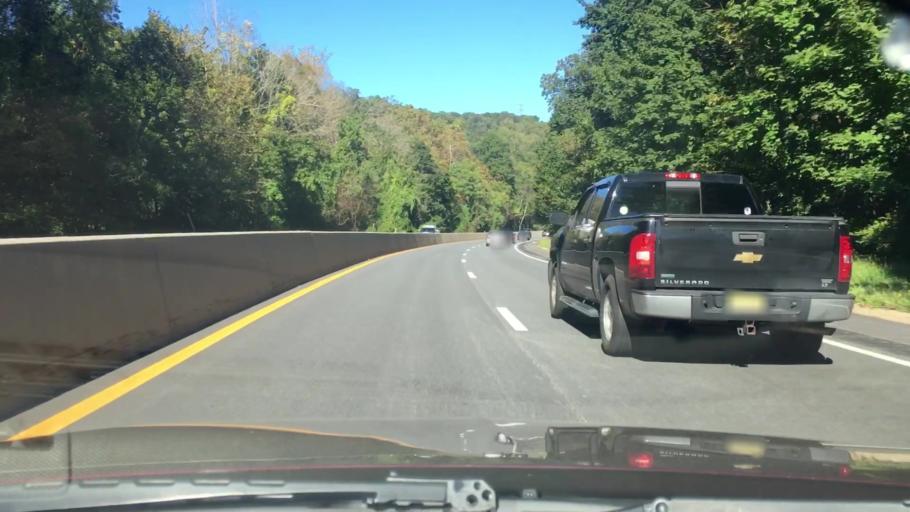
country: US
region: New York
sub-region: Westchester County
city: Pleasantville
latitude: 41.1398
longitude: -73.7924
